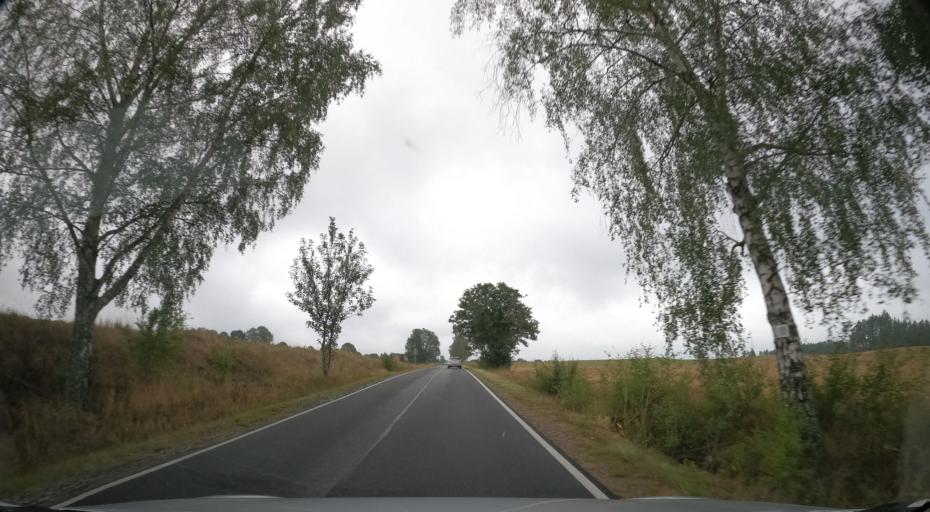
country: PL
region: Pomeranian Voivodeship
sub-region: Powiat wejherowski
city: Linia
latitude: 54.4843
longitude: 17.8484
